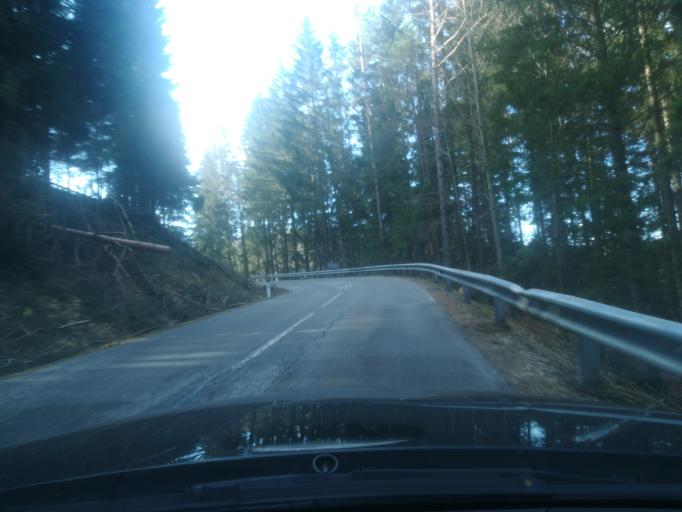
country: AT
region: Lower Austria
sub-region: Politischer Bezirk Zwettl
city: Langschlag
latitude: 48.4599
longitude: 14.7090
